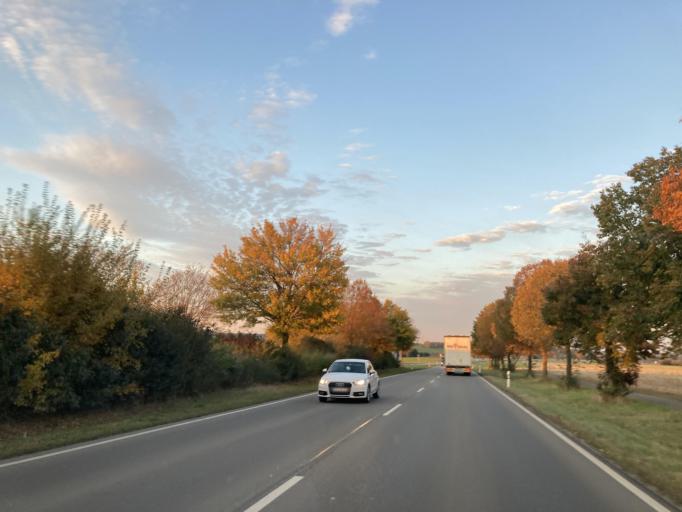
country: DE
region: Baden-Wuerttemberg
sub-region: Tuebingen Region
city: Dotternhausen
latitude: 48.2390
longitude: 8.7999
